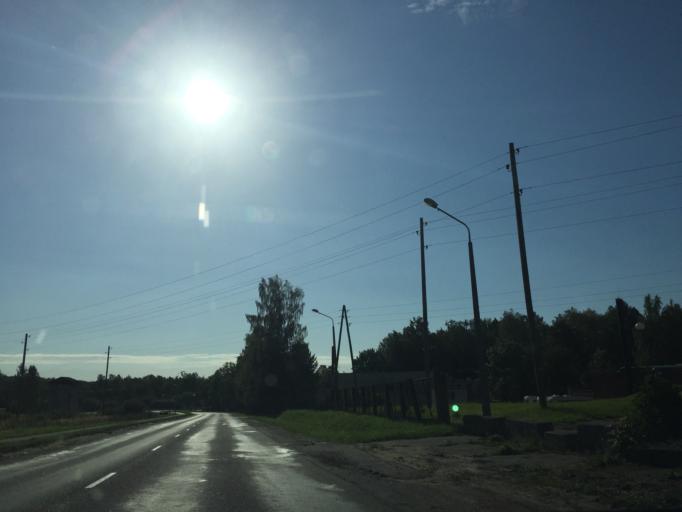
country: LV
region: Limbazu Rajons
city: Limbazi
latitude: 57.5110
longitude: 24.6943
